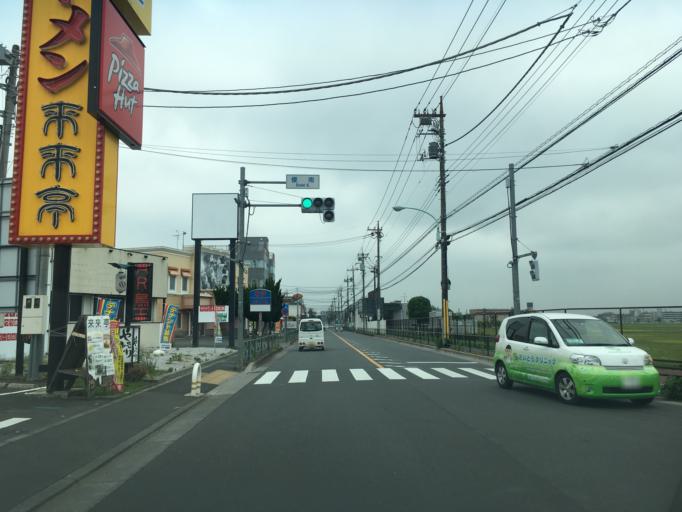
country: JP
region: Tokyo
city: Hino
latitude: 35.7406
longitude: 139.3937
